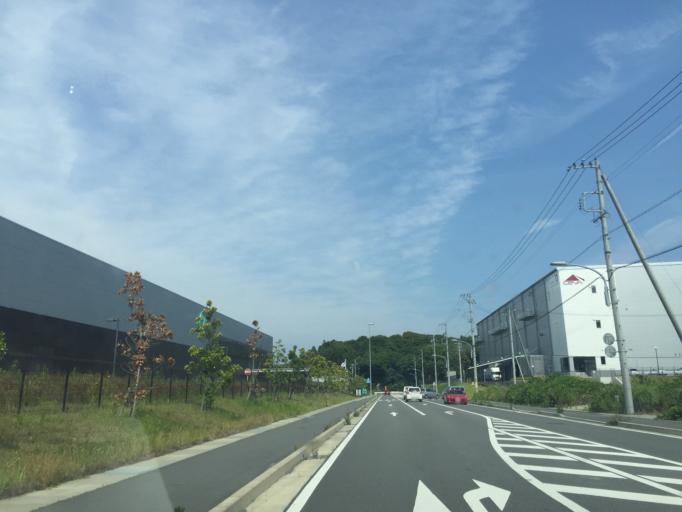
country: JP
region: Shizuoka
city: Kakegawa
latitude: 34.7582
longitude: 138.0013
